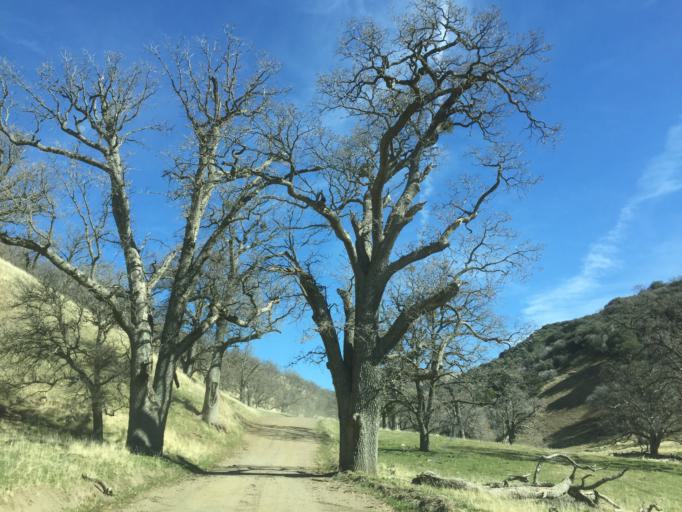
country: US
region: California
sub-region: Kern County
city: Lebec
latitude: 34.9087
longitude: -118.7090
